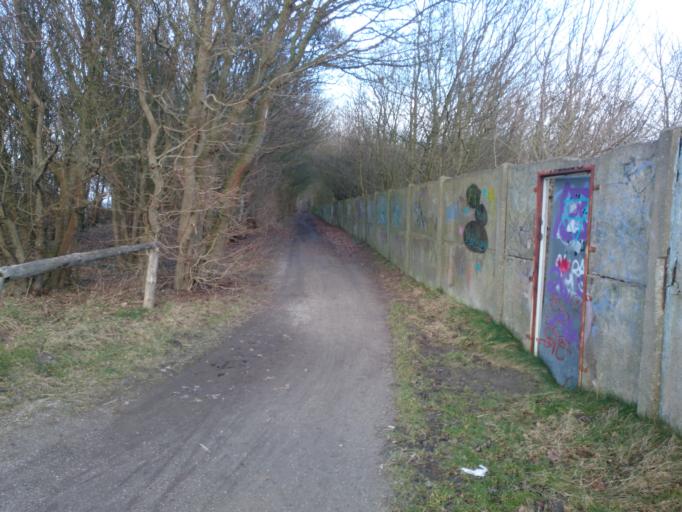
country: DE
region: Mecklenburg-Vorpommern
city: Elmenhorst
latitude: 54.1706
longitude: 11.9819
